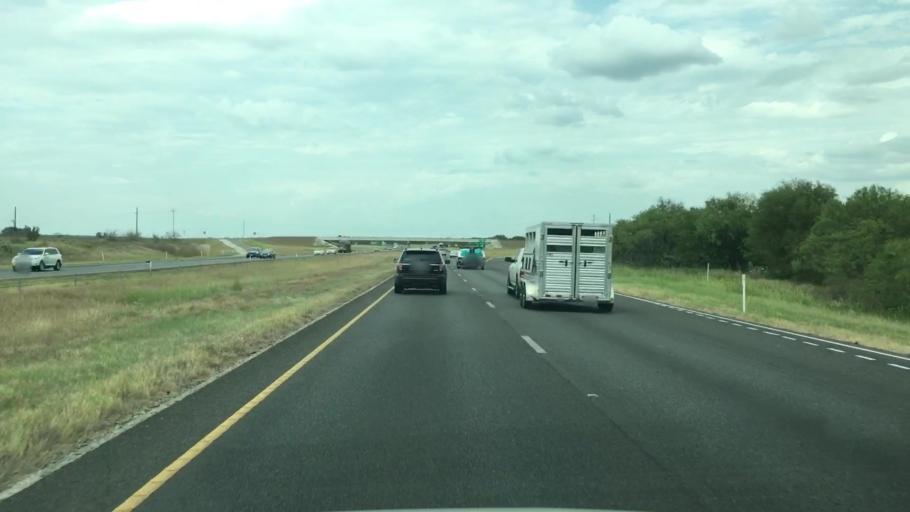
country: US
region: Texas
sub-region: Bexar County
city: Elmendorf
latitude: 29.1379
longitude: -98.4291
